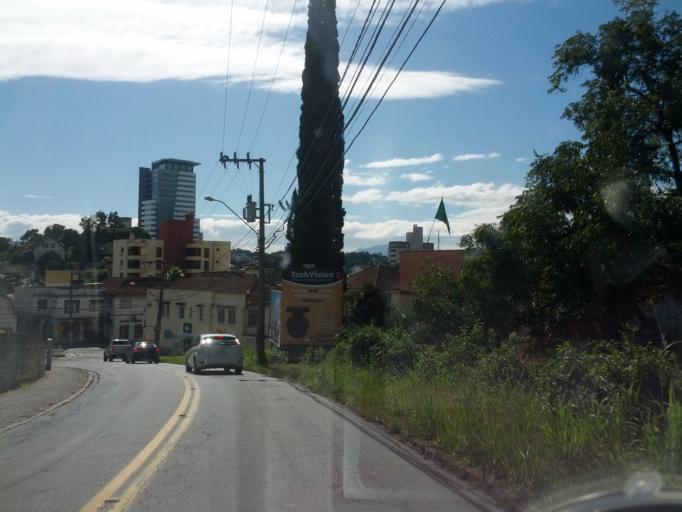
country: BR
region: Santa Catarina
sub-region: Blumenau
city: Blumenau
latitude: -26.9190
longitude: -49.0881
